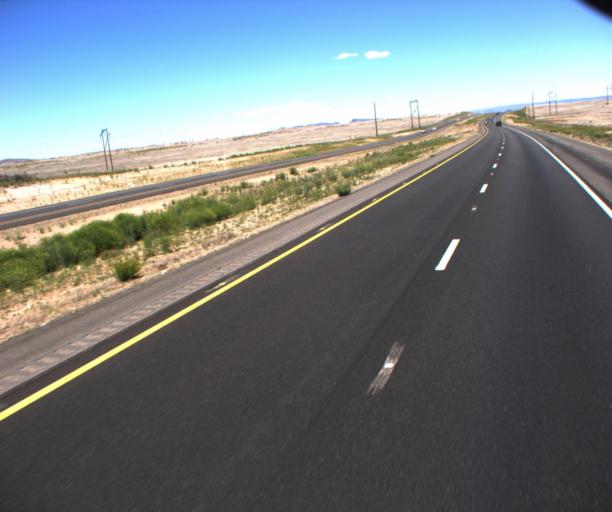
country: US
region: Arizona
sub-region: Yavapai County
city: Chino Valley
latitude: 34.6739
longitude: -112.4409
